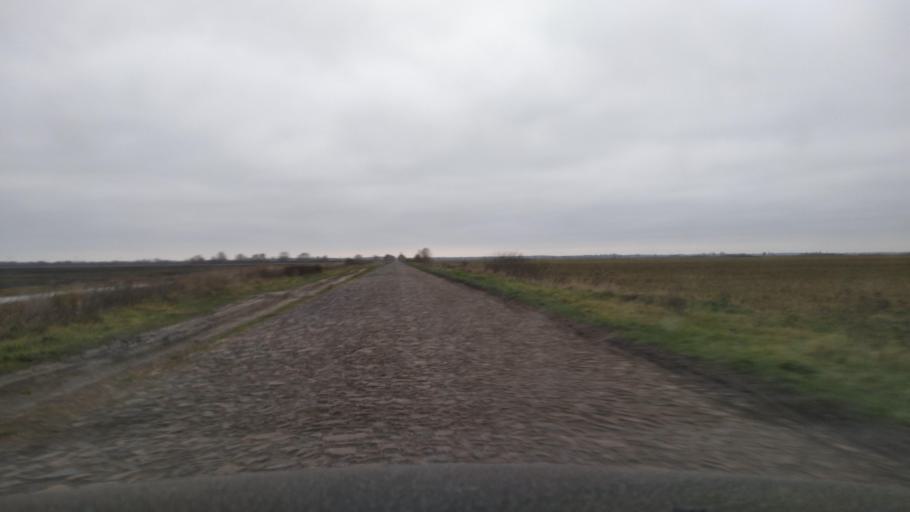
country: BY
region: Brest
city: Davyd-Haradok
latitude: 52.0116
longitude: 27.2056
